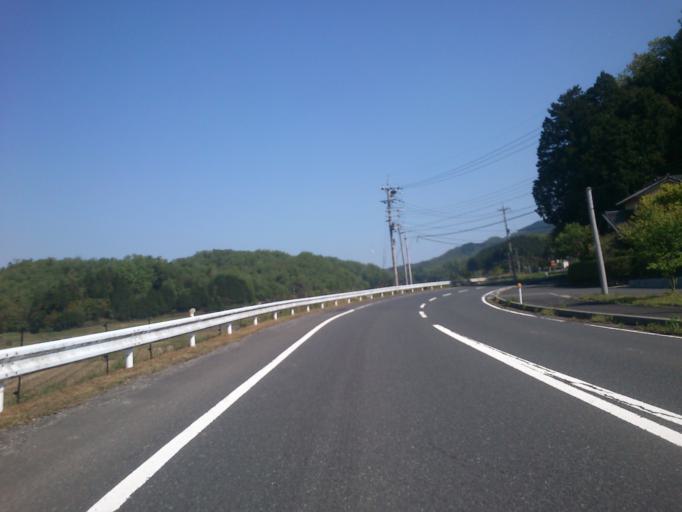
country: JP
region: Kyoto
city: Miyazu
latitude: 35.5988
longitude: 135.1394
